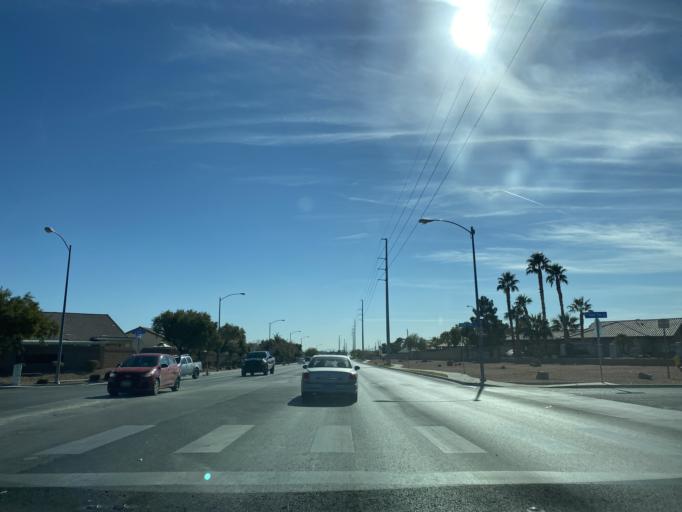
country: US
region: Nevada
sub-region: Clark County
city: North Las Vegas
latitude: 36.2471
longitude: -115.1438
